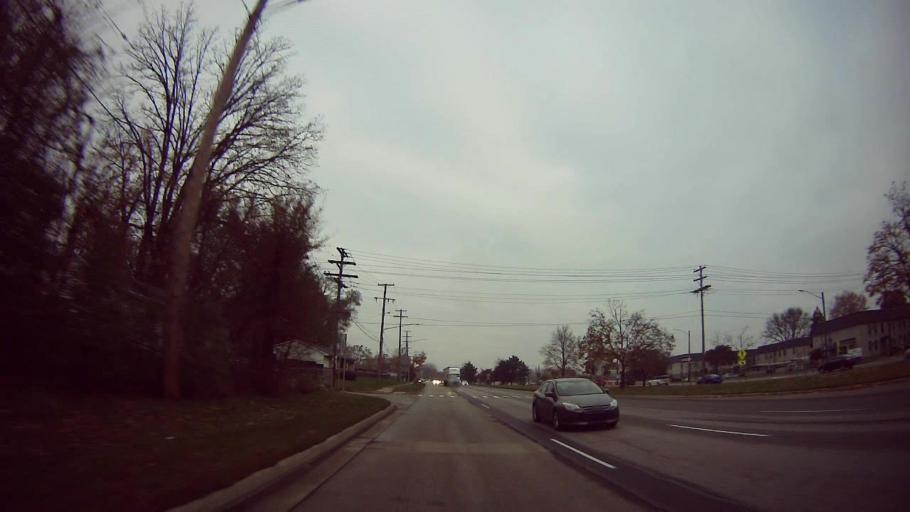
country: US
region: Michigan
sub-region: Wayne County
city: Redford
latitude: 42.4349
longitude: -83.2784
